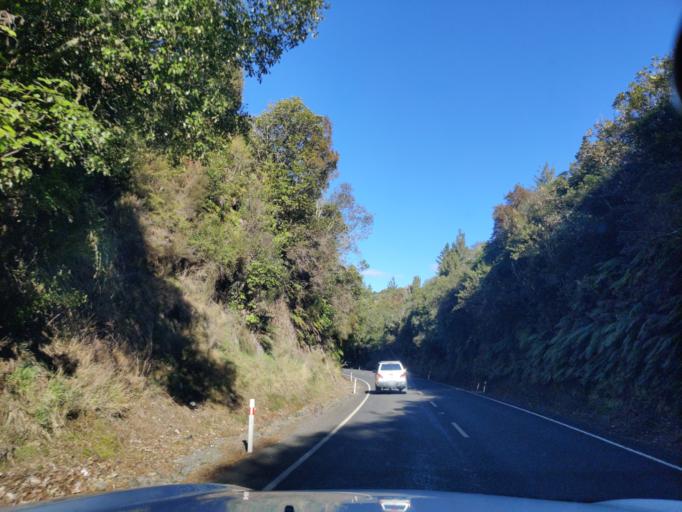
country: NZ
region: Waikato
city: Turangi
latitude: -38.7526
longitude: 175.6757
